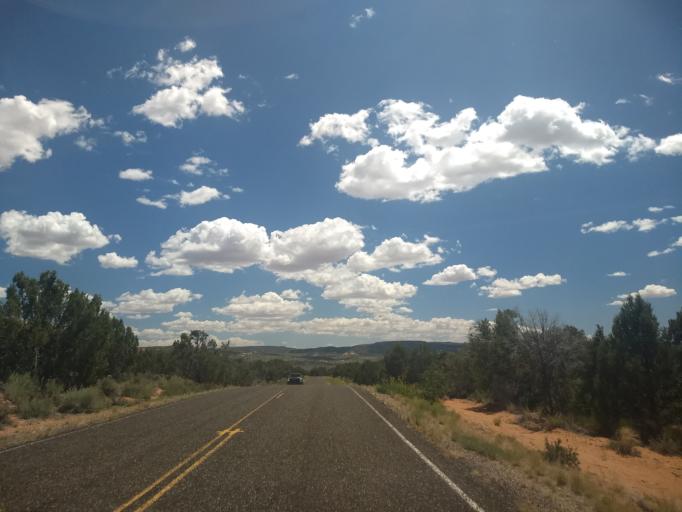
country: US
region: Utah
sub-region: Kane County
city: Kanab
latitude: 37.1829
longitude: -112.6550
